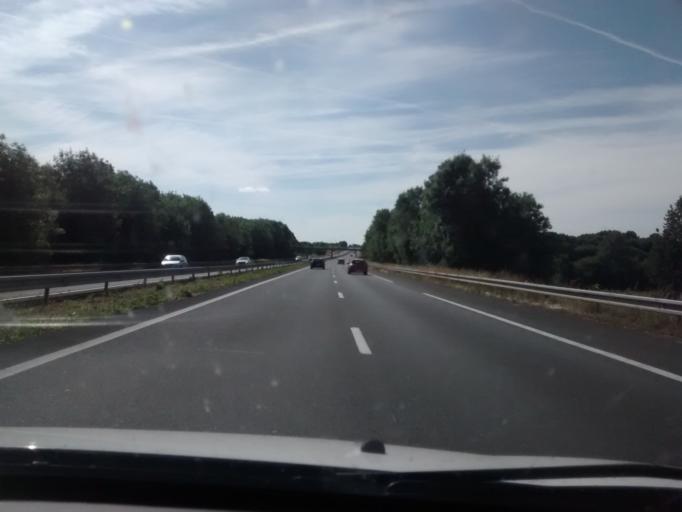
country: FR
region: Pays de la Loire
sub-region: Departement de la Mayenne
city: Soulge-sur-Ouette
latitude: 48.0621
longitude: -0.5256
